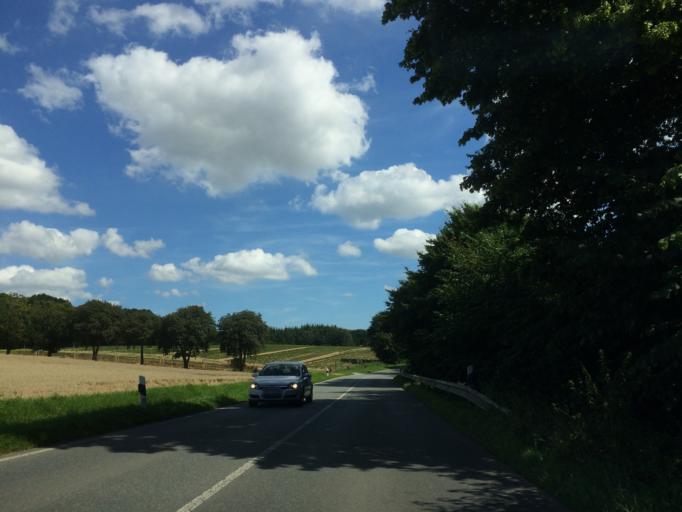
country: DE
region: Schleswig-Holstein
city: Malente
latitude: 54.1613
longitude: 10.5867
